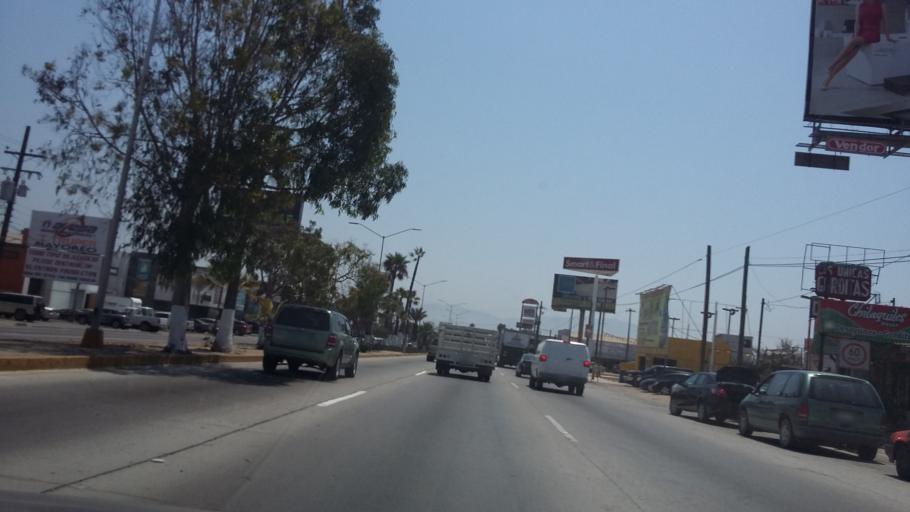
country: MX
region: Baja California
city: Ensenada
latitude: 31.8364
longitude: -116.6019
